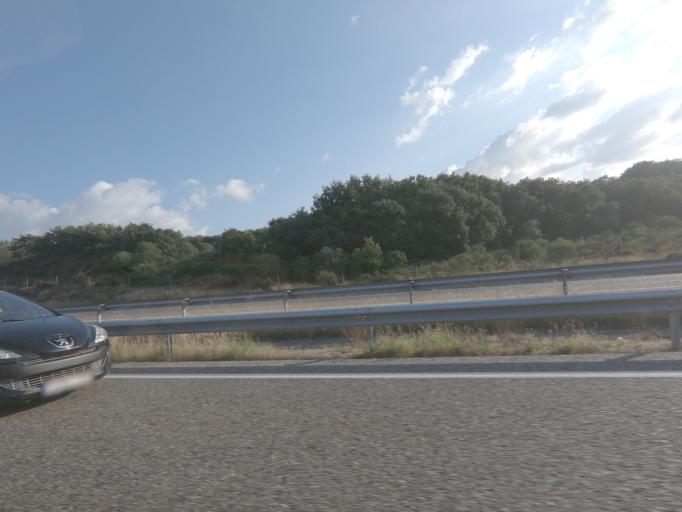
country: ES
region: Galicia
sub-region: Provincia de Ourense
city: Cualedro
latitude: 42.0021
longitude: -7.5620
